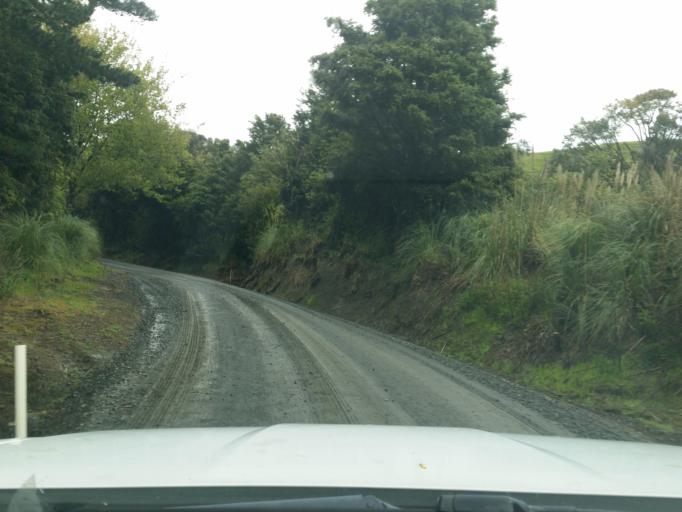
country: NZ
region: Northland
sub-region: Kaipara District
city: Dargaville
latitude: -35.7969
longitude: 173.9874
